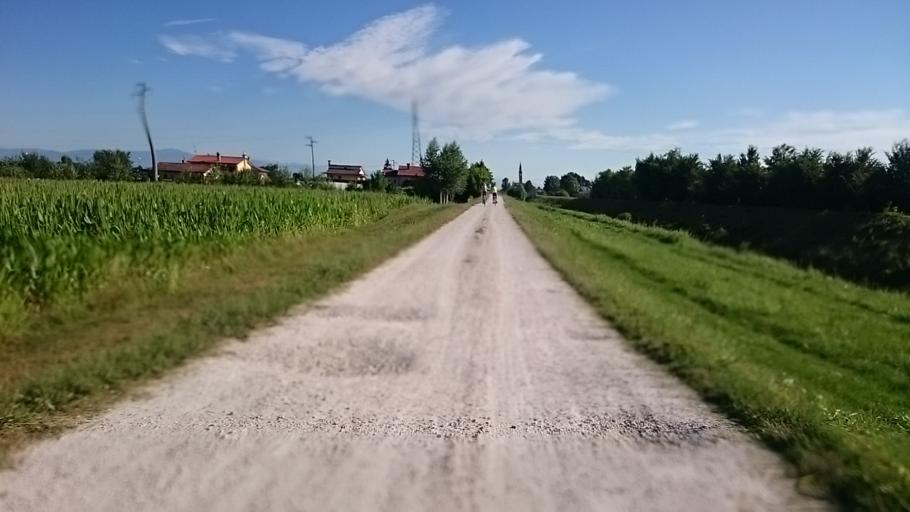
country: IT
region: Veneto
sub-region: Provincia di Padova
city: Campodarsego
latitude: 45.4896
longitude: 11.9019
